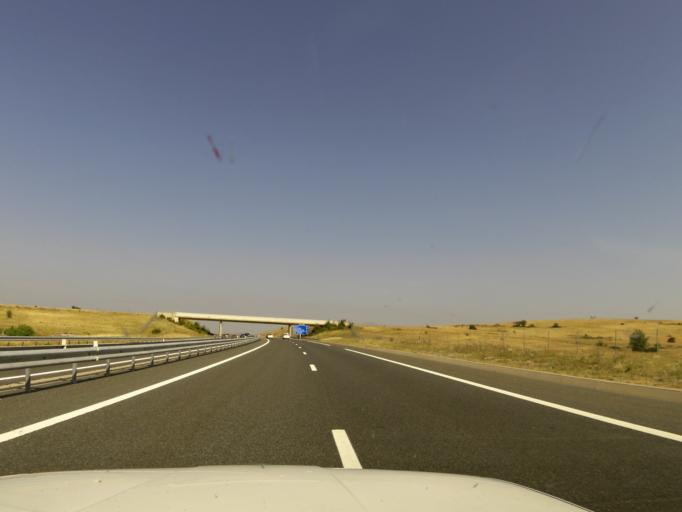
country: FR
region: Midi-Pyrenees
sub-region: Departement de l'Aveyron
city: Creissels
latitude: 44.0272
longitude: 3.0741
